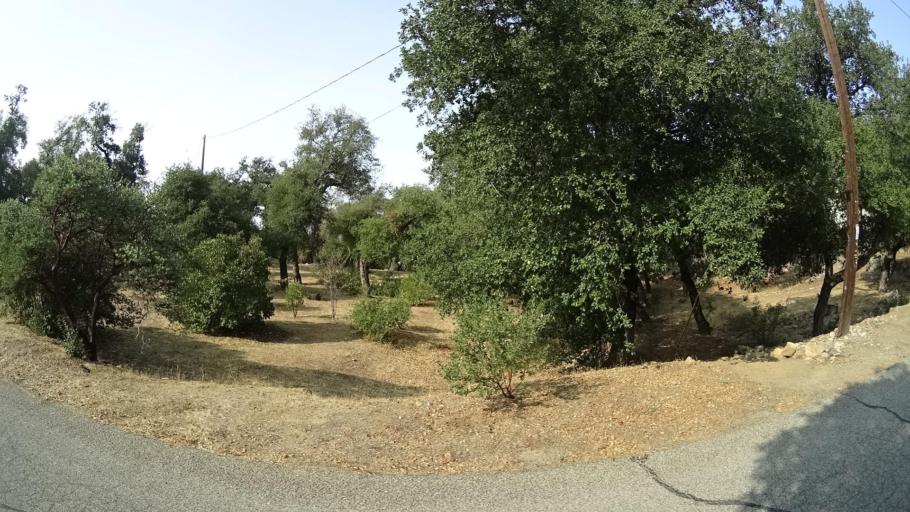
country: US
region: California
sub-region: San Diego County
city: Julian
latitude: 33.0965
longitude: -116.6577
